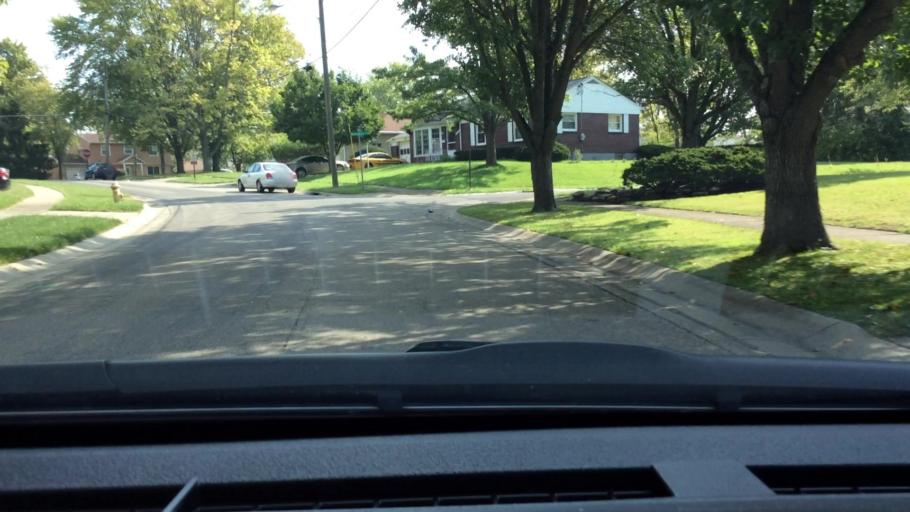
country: US
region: Ohio
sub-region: Hamilton County
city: Forest Park
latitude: 39.2691
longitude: -84.5012
